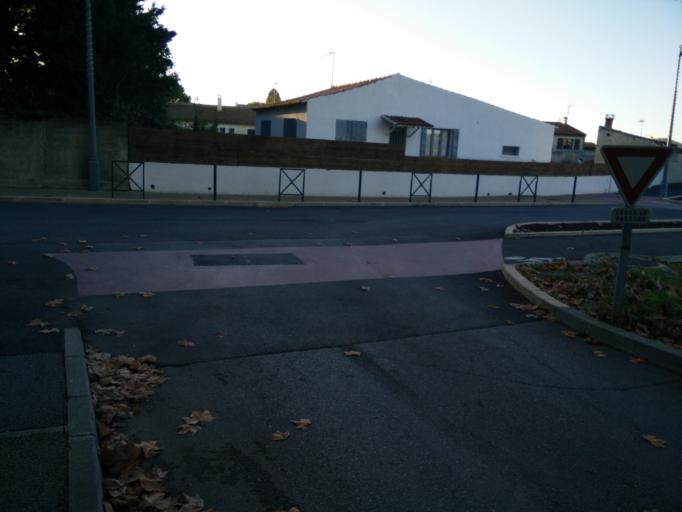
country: FR
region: Languedoc-Roussillon
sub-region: Departement du Gard
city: Aimargues
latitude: 43.6905
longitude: 4.2064
